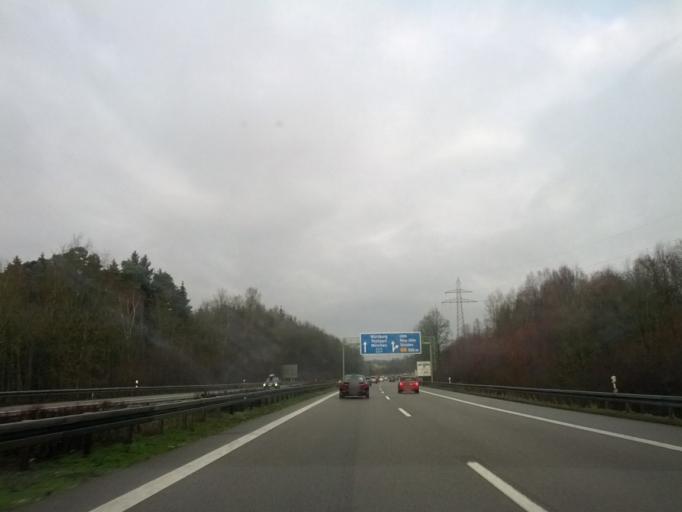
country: DE
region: Bavaria
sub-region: Swabia
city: Vohringen
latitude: 48.3129
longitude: 10.0944
